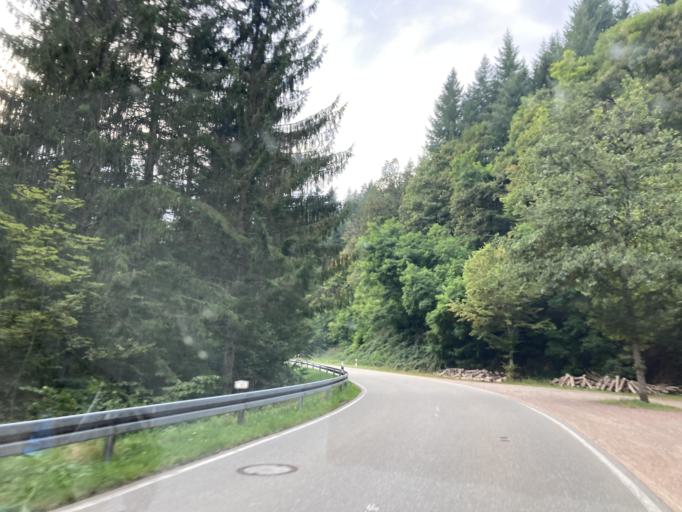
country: DE
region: Baden-Wuerttemberg
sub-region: Freiburg Region
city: Wembach
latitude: 47.7776
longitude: 7.8738
